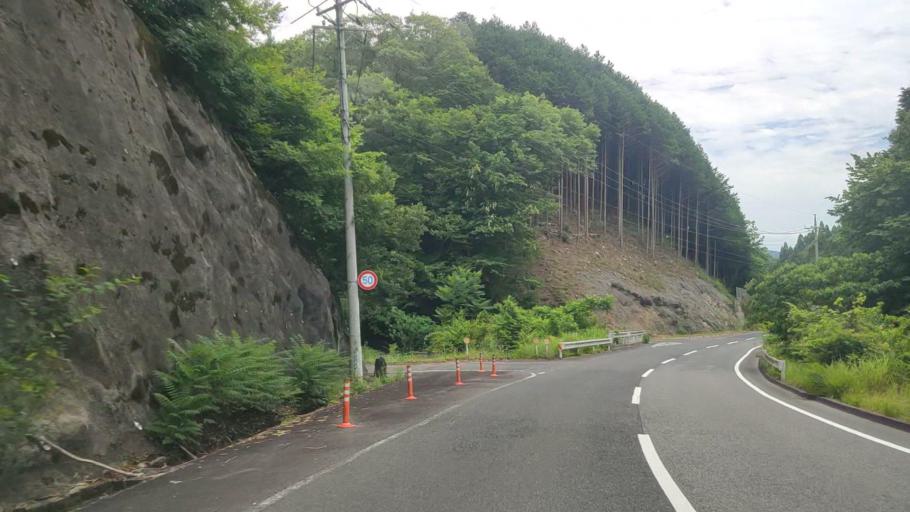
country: JP
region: Okayama
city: Tsuyama
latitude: 35.0994
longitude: 134.2773
